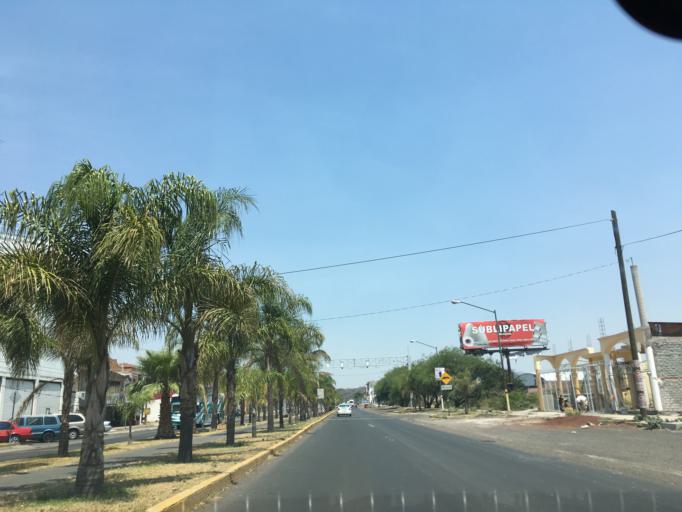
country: MX
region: Guanajuato
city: Moroleon
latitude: 20.1027
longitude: -101.1639
